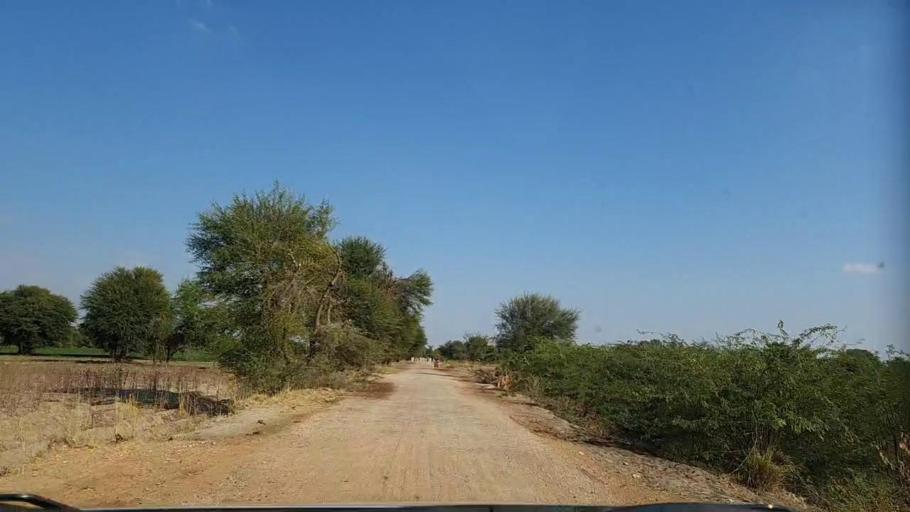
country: PK
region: Sindh
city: Pithoro
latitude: 25.6346
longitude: 69.3567
